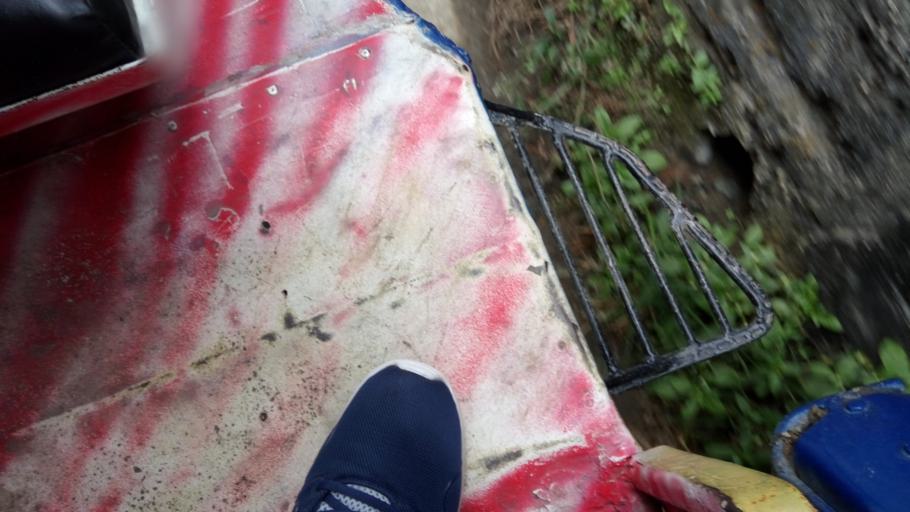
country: PH
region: Ilocos
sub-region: Province of La Union
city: Payocpoc Sur
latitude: 16.4653
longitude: 120.3342
